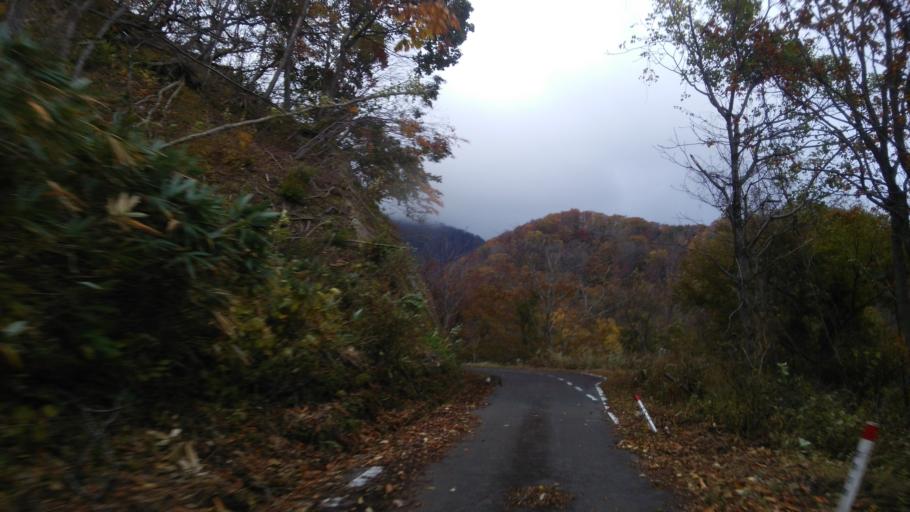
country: JP
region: Fukushima
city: Kitakata
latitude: 37.3875
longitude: 139.7244
